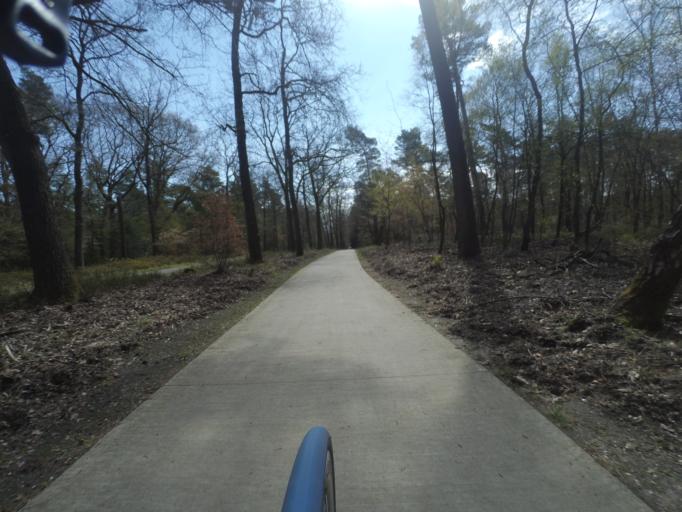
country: NL
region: Gelderland
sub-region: Gemeente Nunspeet
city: Nunspeet
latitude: 52.3403
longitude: 5.8694
